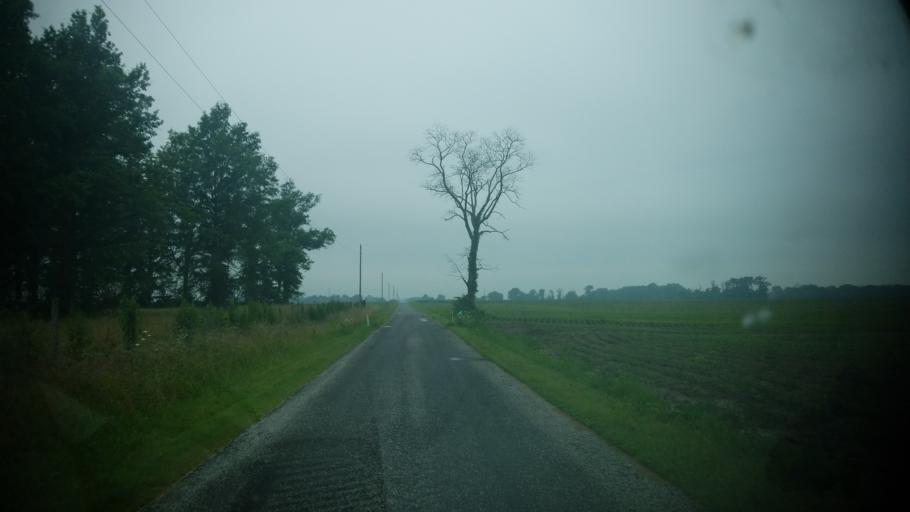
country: US
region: Illinois
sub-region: Clay County
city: Flora
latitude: 38.5736
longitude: -88.3931
